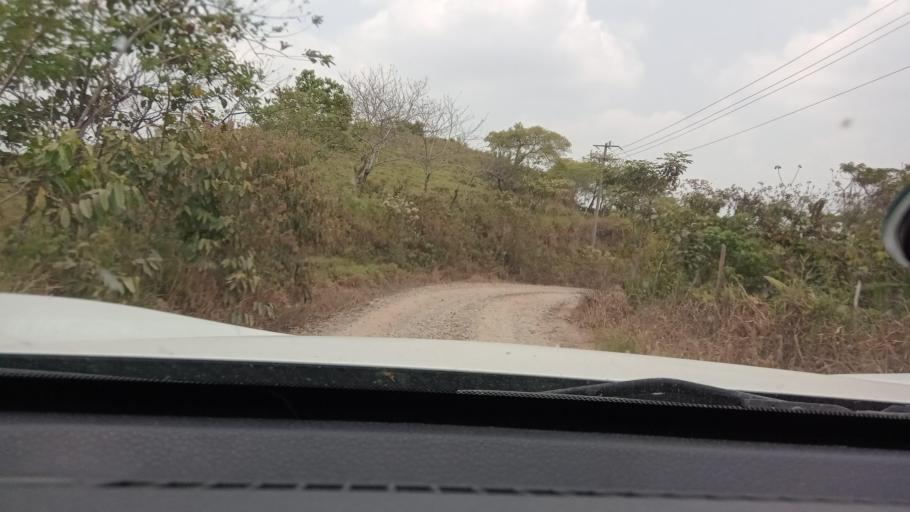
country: MX
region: Tabasco
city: Chontalpa
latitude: 17.5744
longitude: -93.7081
